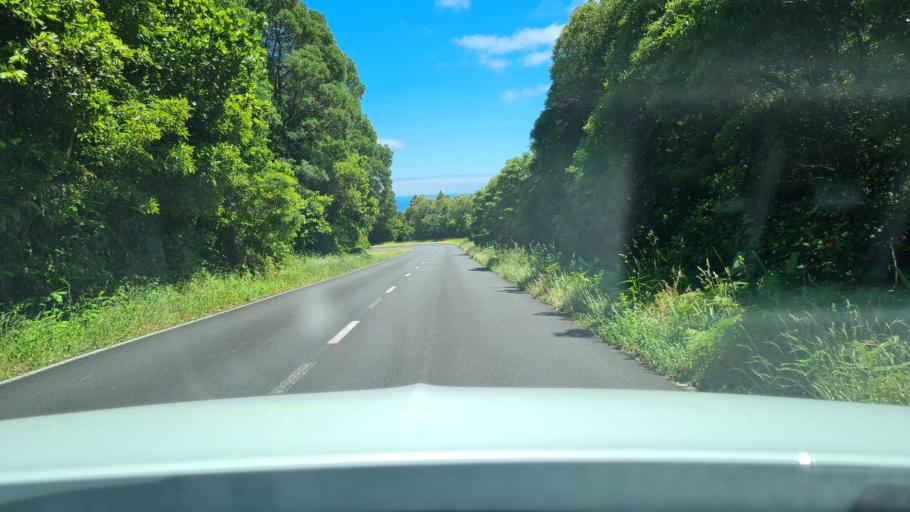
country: PT
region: Azores
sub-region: Sao Roque do Pico
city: Sao Roque do Pico
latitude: 38.4277
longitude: -28.2911
